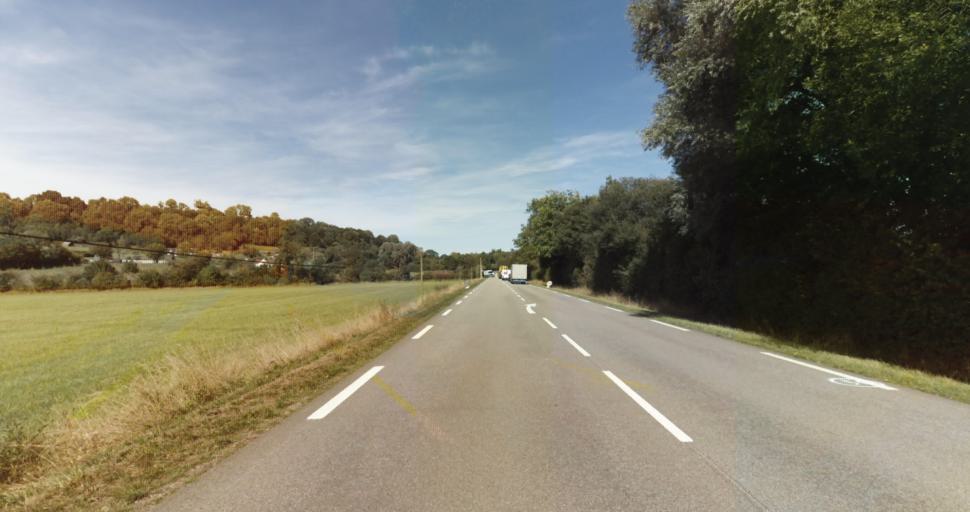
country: FR
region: Lower Normandy
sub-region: Departement de l'Orne
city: Gace
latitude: 48.7253
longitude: 0.2339
